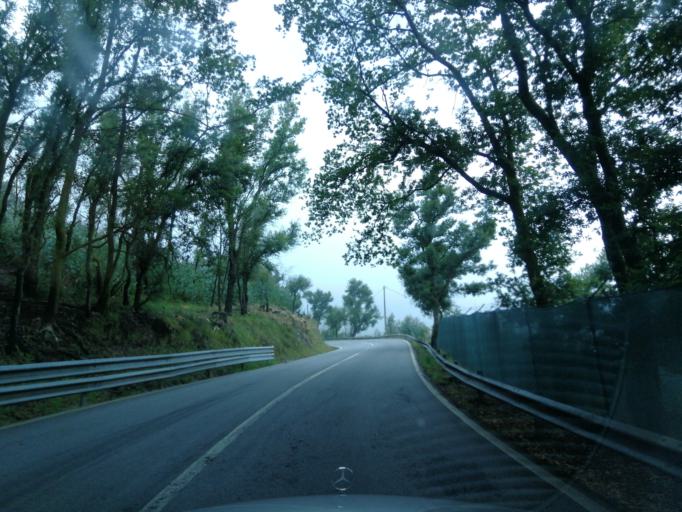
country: PT
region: Braga
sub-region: Braga
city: Braga
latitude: 41.5242
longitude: -8.3886
